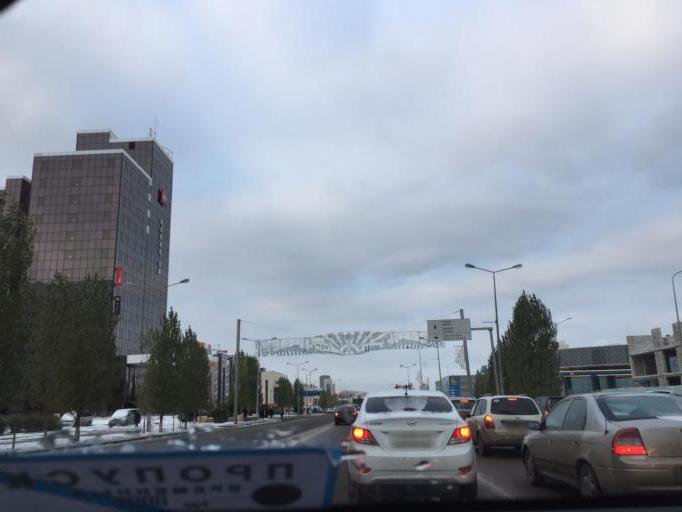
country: KZ
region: Astana Qalasy
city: Astana
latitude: 51.1376
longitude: 71.4695
